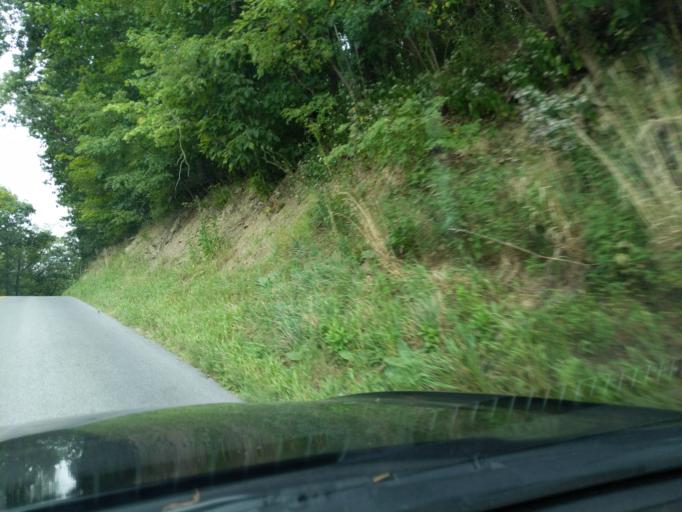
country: US
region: Pennsylvania
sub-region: Blair County
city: Claysburg
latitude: 40.3551
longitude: -78.4660
